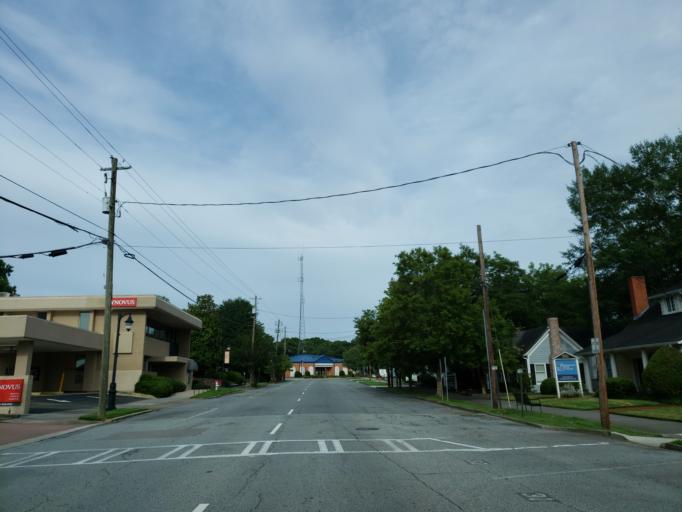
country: US
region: Georgia
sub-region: Cherokee County
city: Canton
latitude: 34.2367
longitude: -84.4892
